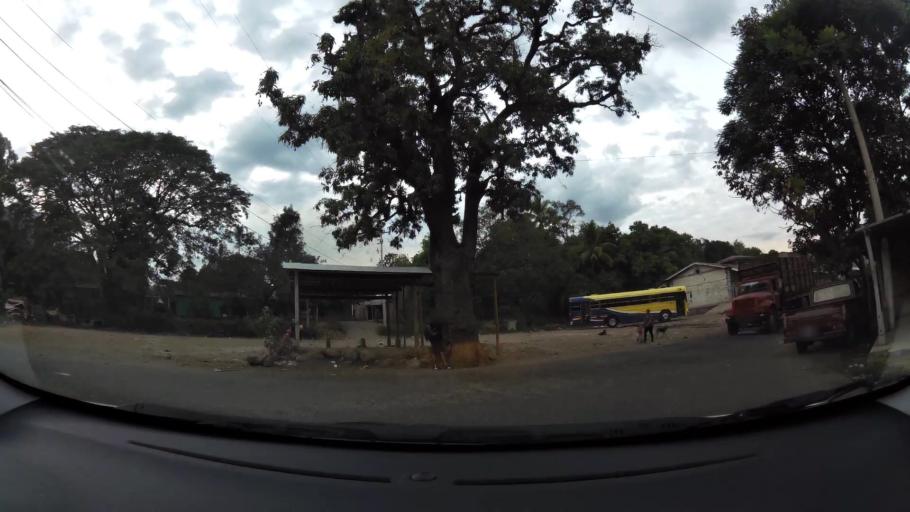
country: SV
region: San Vicente
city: San Vicente
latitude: 13.6422
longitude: -88.7927
